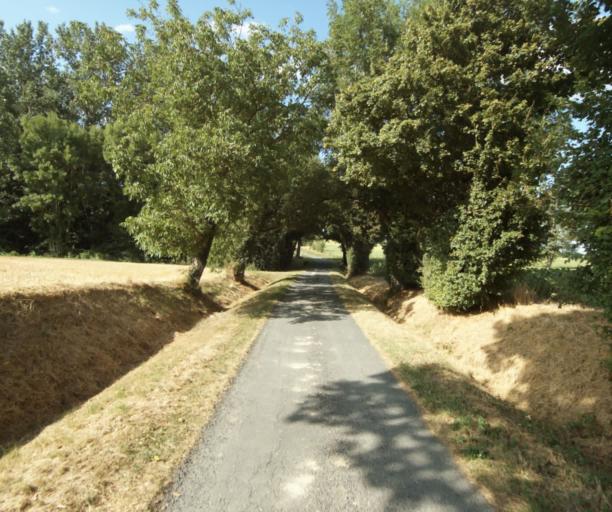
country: FR
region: Midi-Pyrenees
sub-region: Departement du Tarn
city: Puylaurens
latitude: 43.5321
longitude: 1.9824
